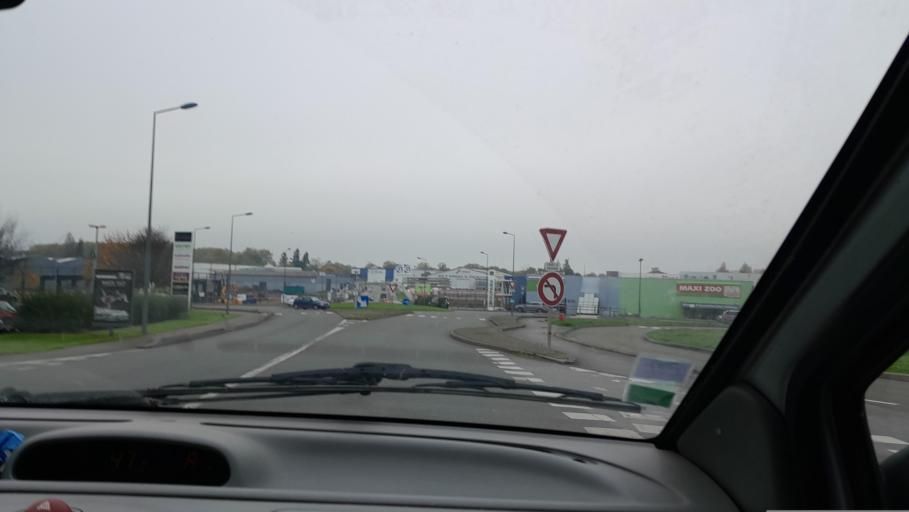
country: FR
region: Pays de la Loire
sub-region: Departement de la Mayenne
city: Saint-Berthevin
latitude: 48.0652
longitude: -0.8116
